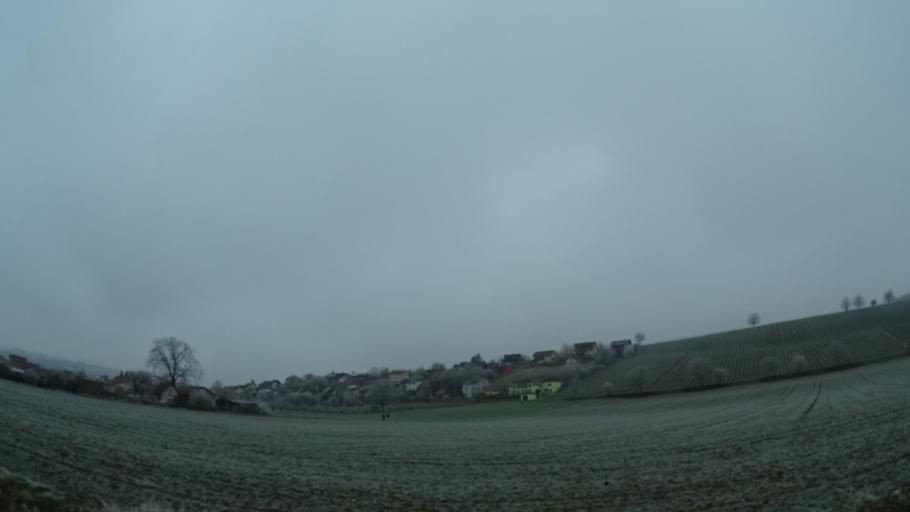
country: DE
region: Bavaria
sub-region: Regierungsbezirk Unterfranken
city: Segnitz
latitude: 49.6790
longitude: 10.1430
